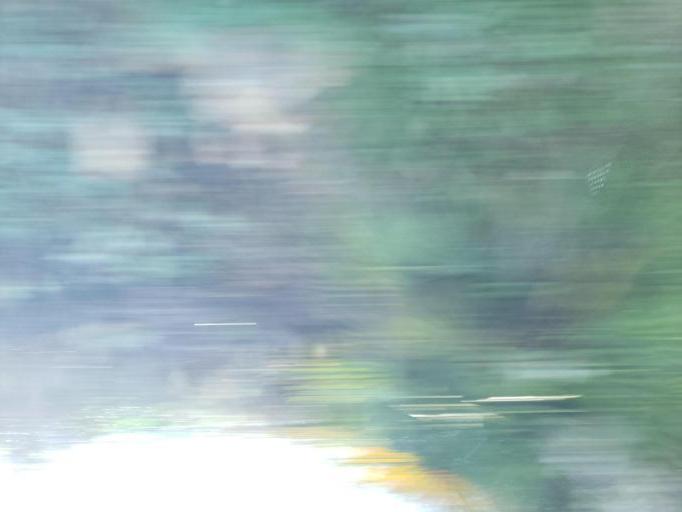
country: PT
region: Faro
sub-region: Portimao
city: Alvor
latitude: 37.1747
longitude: -8.5788
